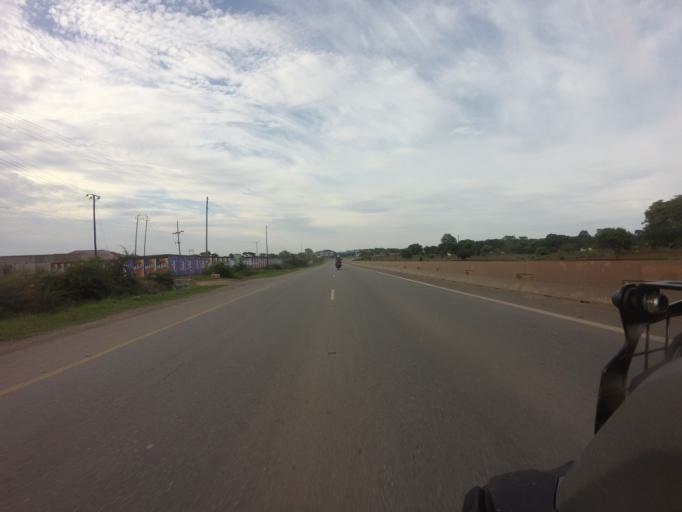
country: ZM
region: Lusaka
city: Lusaka
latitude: -15.5313
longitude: 28.2616
